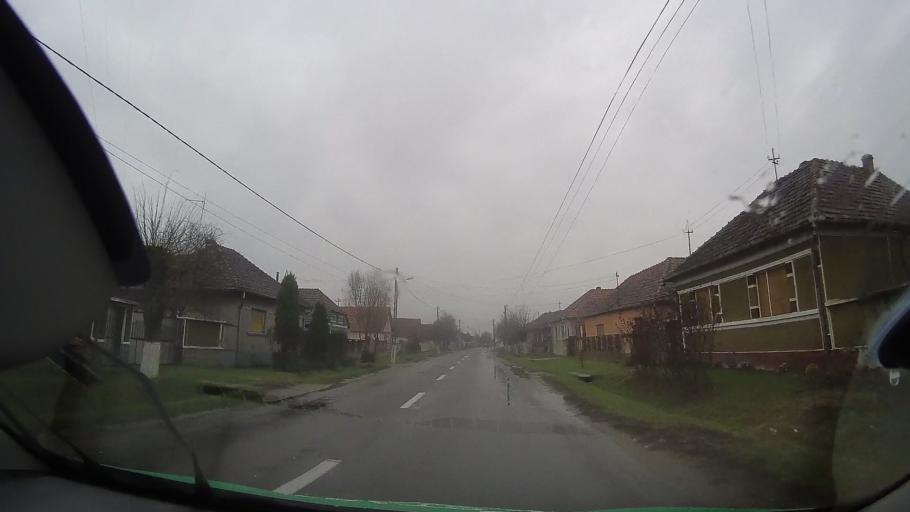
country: RO
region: Bihor
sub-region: Comuna Tinca
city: Gurbediu
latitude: 46.7920
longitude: 21.8591
